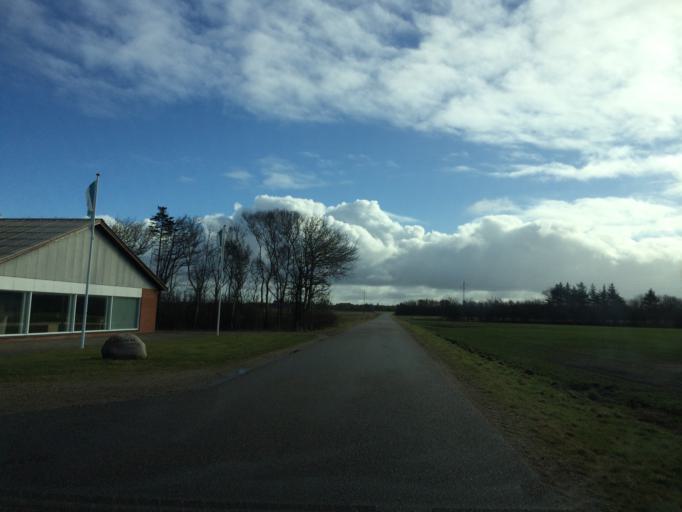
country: DK
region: Central Jutland
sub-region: Holstebro Kommune
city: Ulfborg
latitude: 56.2825
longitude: 8.3304
